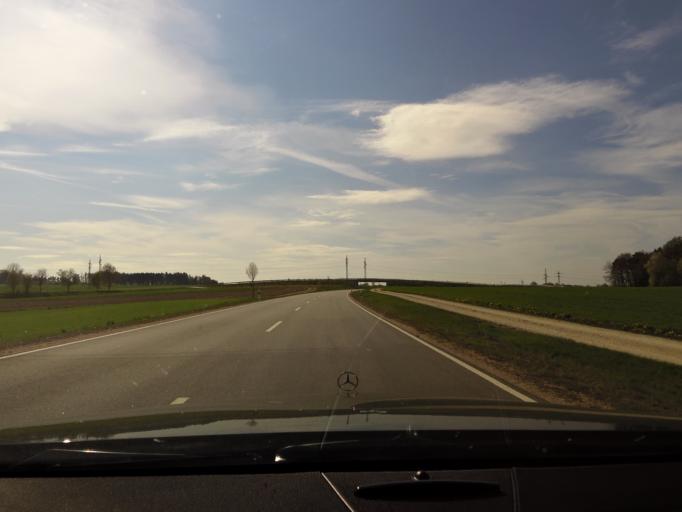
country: DE
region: Bavaria
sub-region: Upper Palatinate
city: Schierling
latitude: 48.8213
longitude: 12.1635
